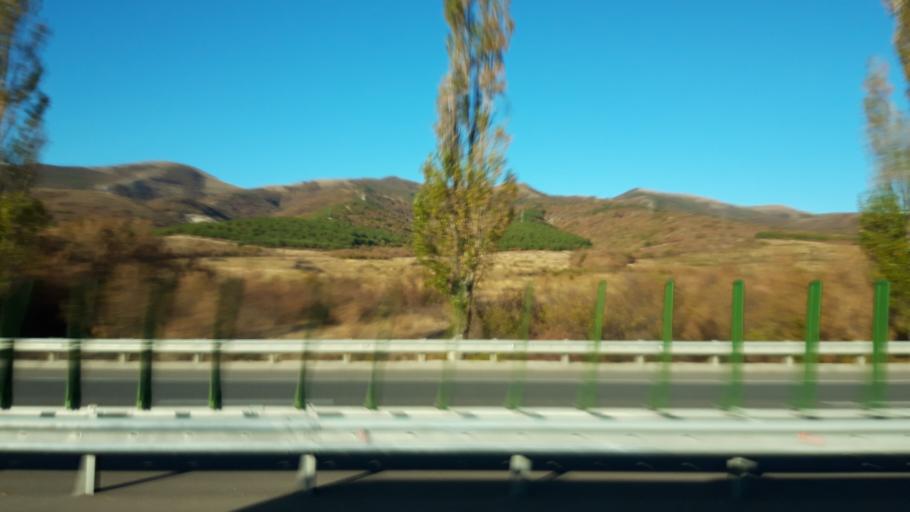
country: RU
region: Krasnodarskiy
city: Kabardinka
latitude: 44.6431
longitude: 37.9711
